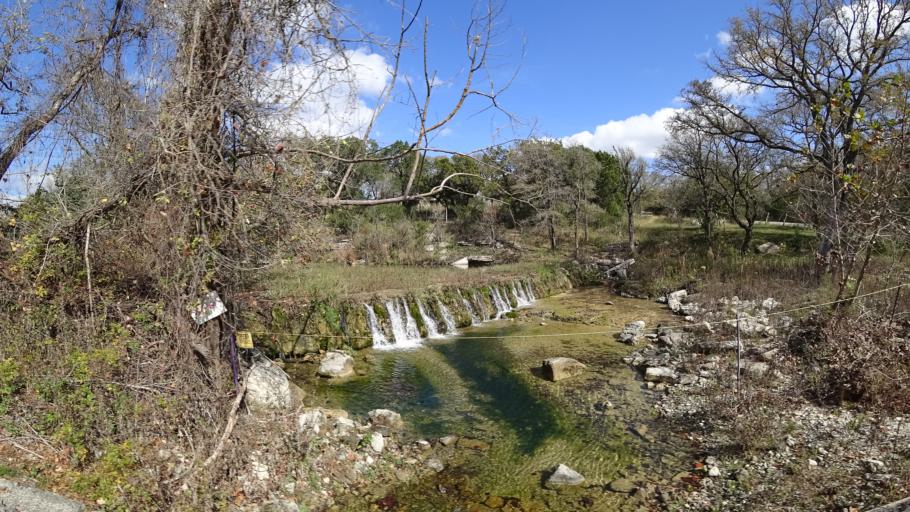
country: US
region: Texas
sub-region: Williamson County
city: Jollyville
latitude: 30.3994
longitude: -97.7830
